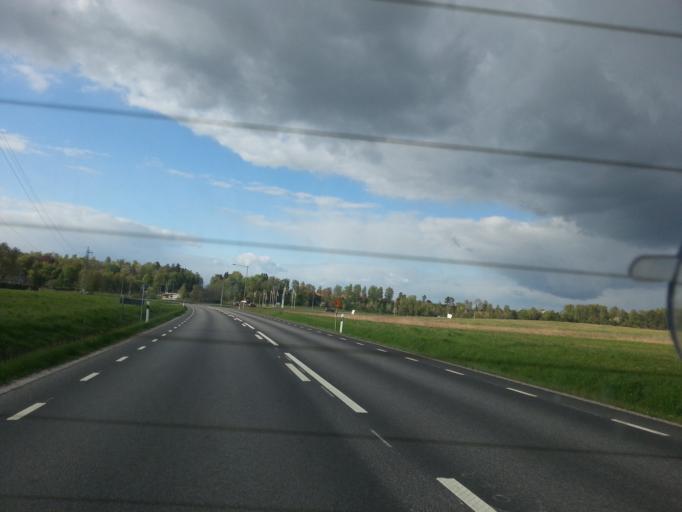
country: SE
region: Skane
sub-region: Sjobo Kommun
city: Sjoebo
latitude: 55.6201
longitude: 13.7057
